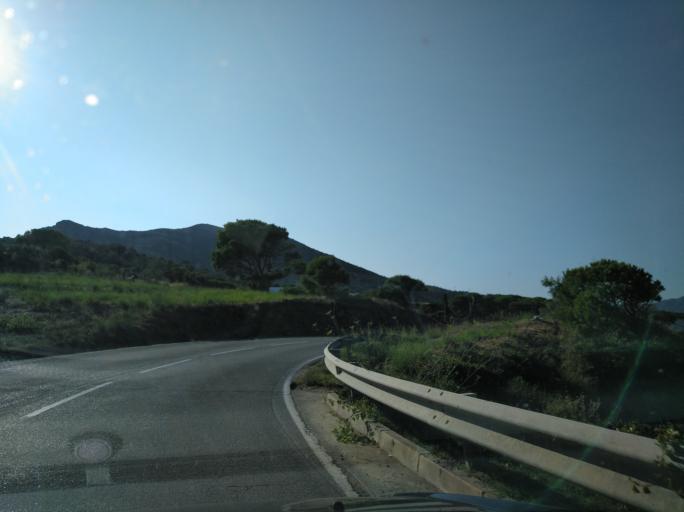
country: ES
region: Catalonia
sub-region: Provincia de Girona
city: Llanca
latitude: 42.3383
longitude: 3.1909
